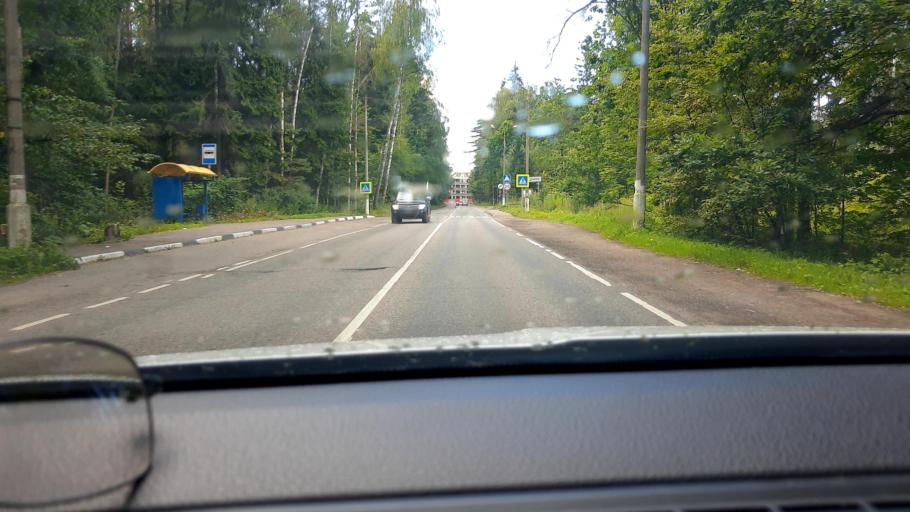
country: RU
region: Moskovskaya
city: Povedniki
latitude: 55.9723
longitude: 37.6097
